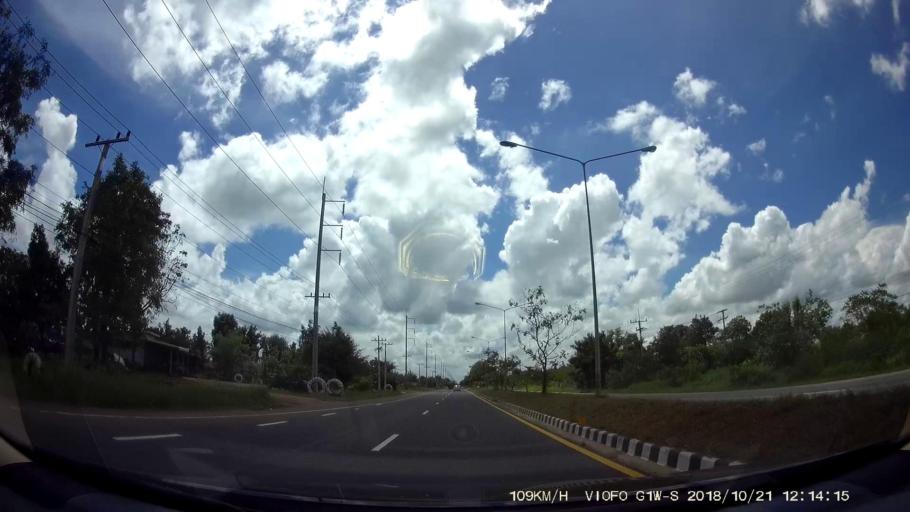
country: TH
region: Nakhon Ratchasima
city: Dan Khun Thot
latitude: 15.3802
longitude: 101.8360
